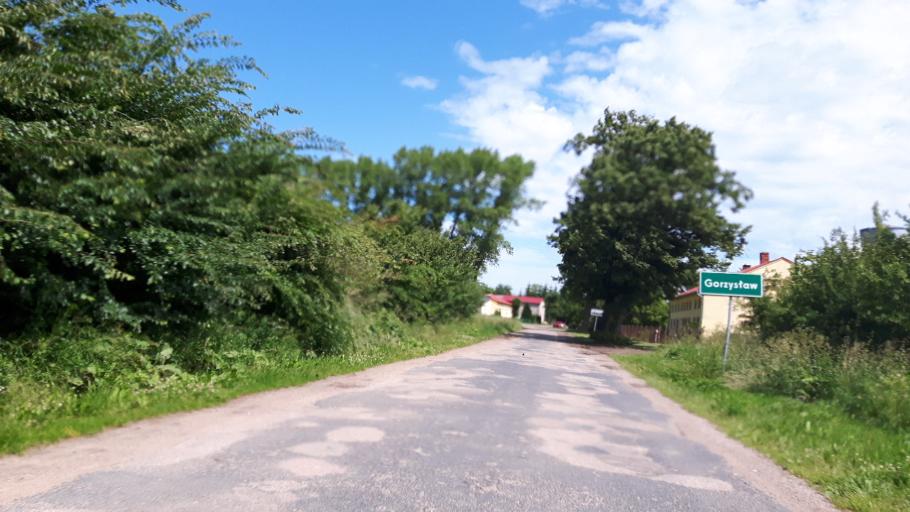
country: PL
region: West Pomeranian Voivodeship
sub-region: Powiat gryficki
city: Trzebiatow
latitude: 54.0870
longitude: 15.2940
